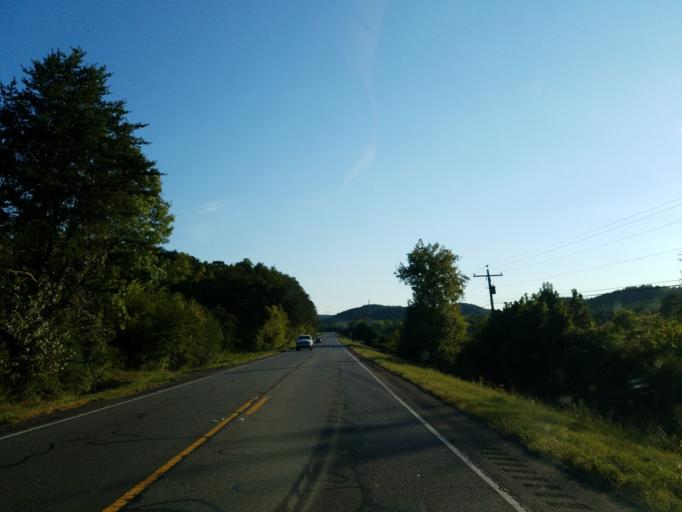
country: US
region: Georgia
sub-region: Bartow County
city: Rydal
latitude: 34.4084
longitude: -84.7029
